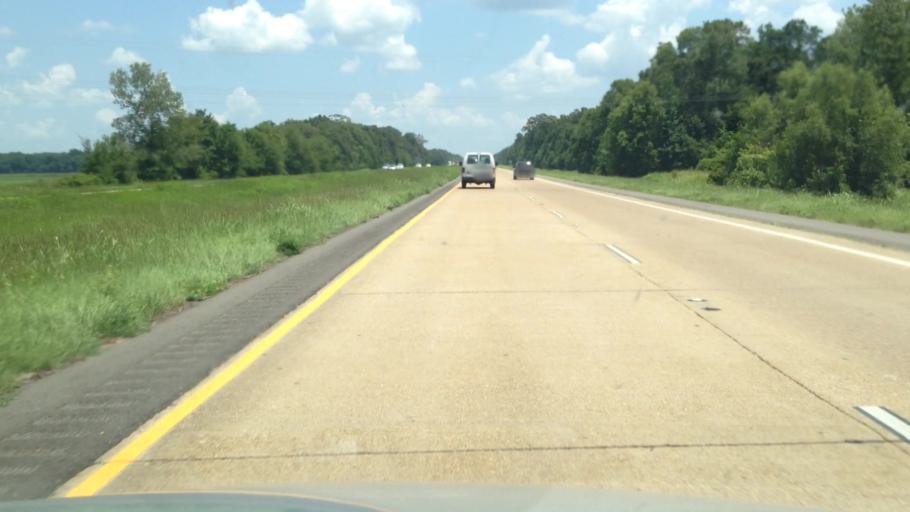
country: US
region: Louisiana
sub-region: Rapides Parish
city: Lecompte
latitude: 31.0022
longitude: -92.3451
